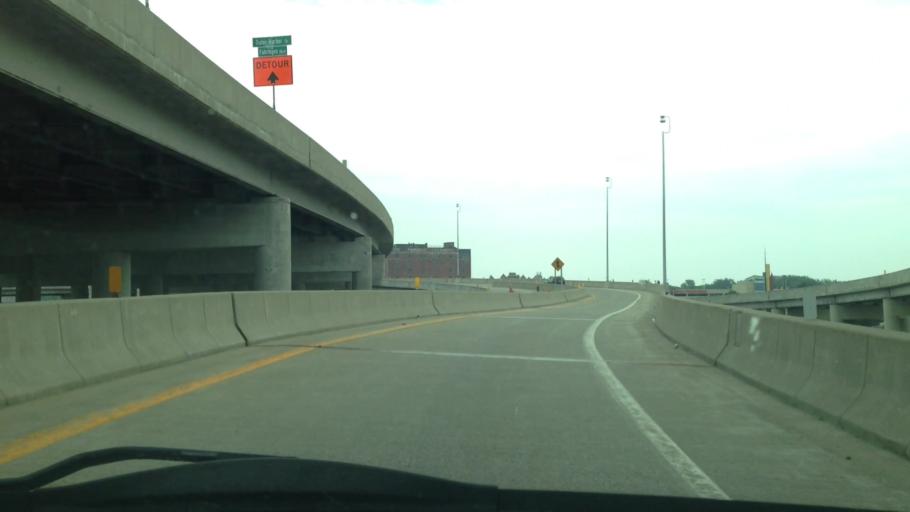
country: US
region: New York
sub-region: Erie County
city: Buffalo
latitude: 42.8777
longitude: -78.8739
